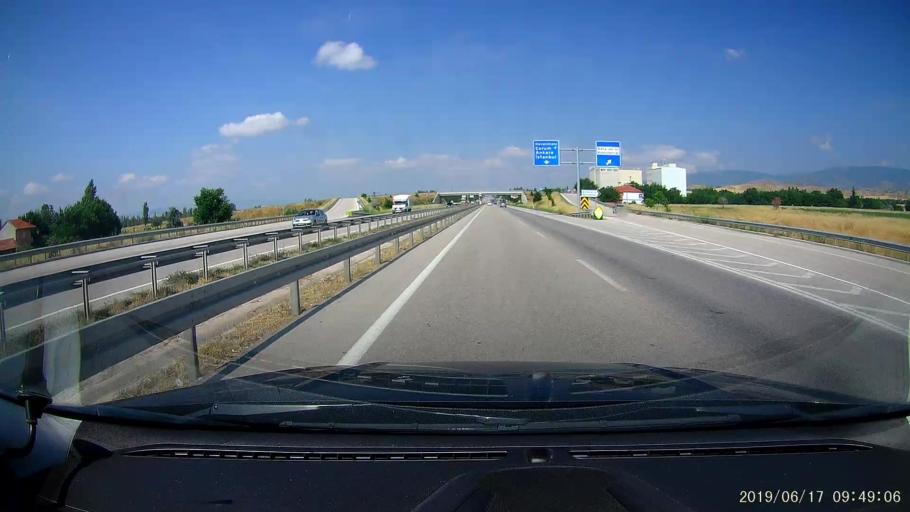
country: TR
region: Amasya
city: Merzifon
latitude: 40.8732
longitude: 35.5358
